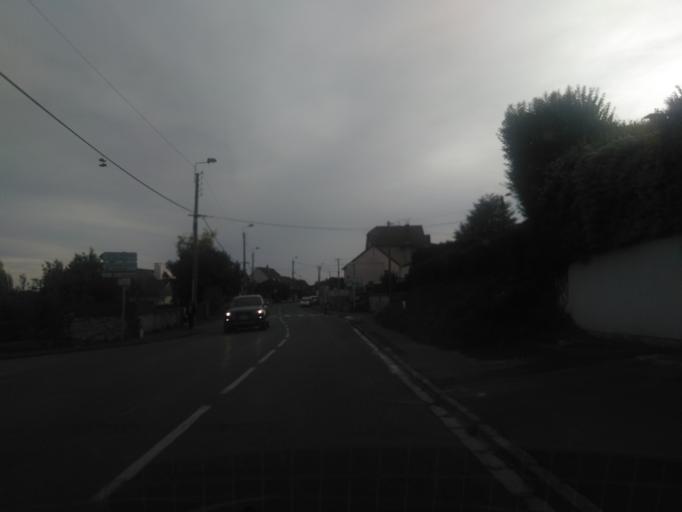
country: FR
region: Picardie
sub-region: Departement de l'Aisne
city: Laon
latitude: 49.5595
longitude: 3.6303
